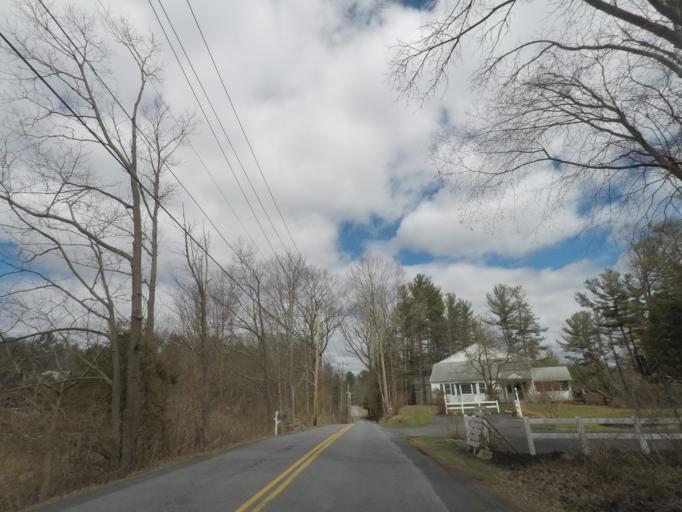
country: US
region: New York
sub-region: Albany County
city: Voorheesville
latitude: 42.6287
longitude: -73.8852
